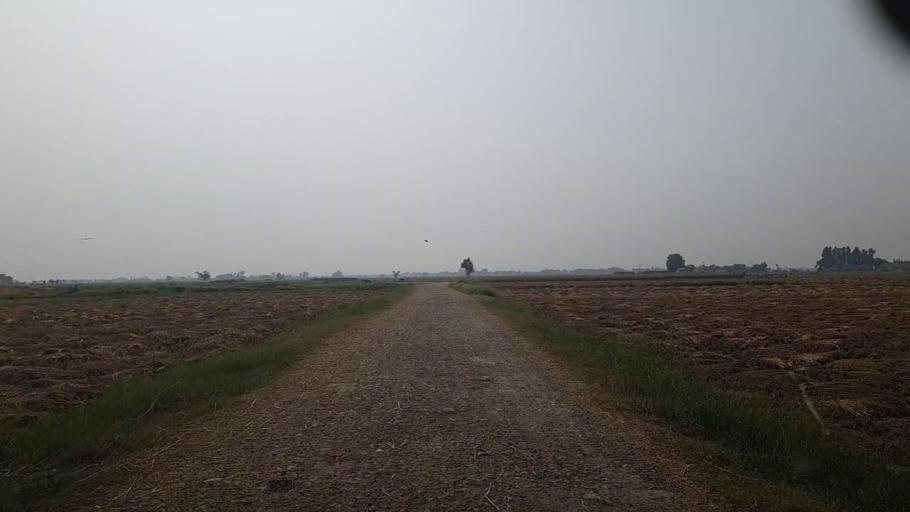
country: PK
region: Sindh
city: Kashmor
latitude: 28.3812
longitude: 69.4302
